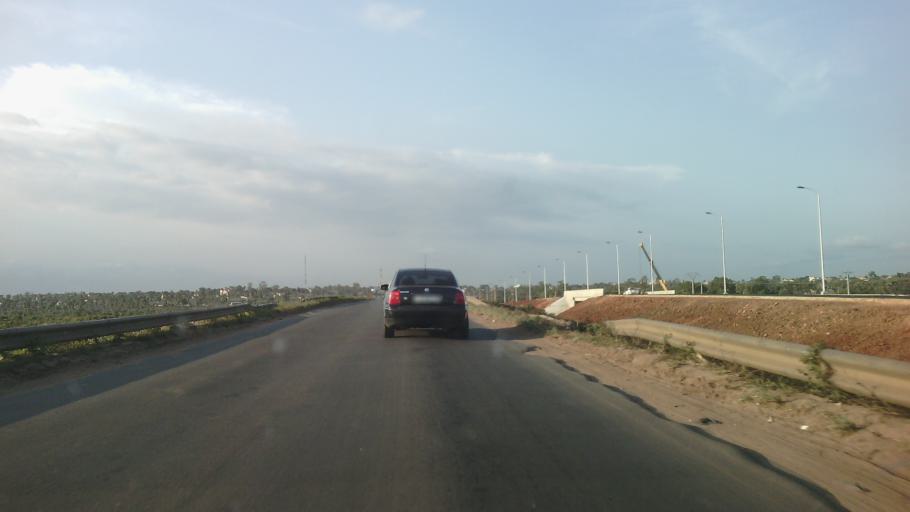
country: TG
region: Maritime
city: Tsevie
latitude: 6.3047
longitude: 1.2149
